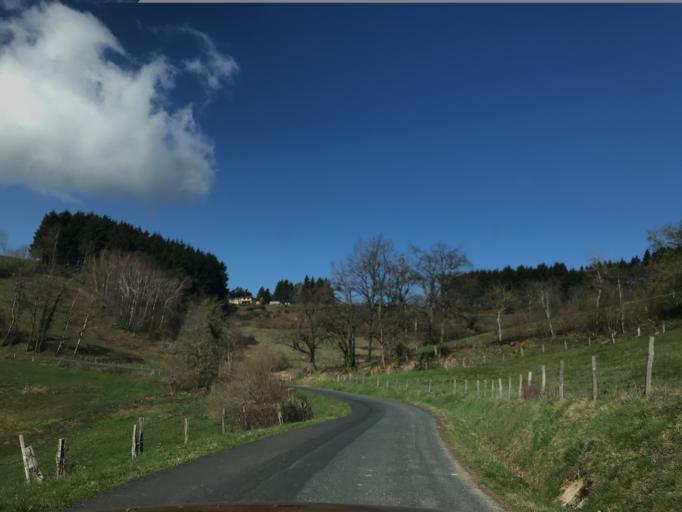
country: FR
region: Auvergne
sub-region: Departement du Puy-de-Dome
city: Escoutoux
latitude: 45.8080
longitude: 3.6055
